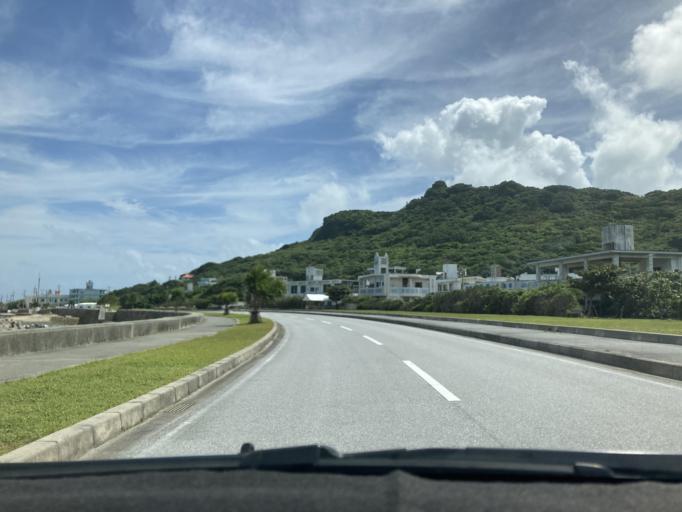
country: JP
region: Okinawa
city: Ginowan
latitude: 26.1802
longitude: 127.8224
